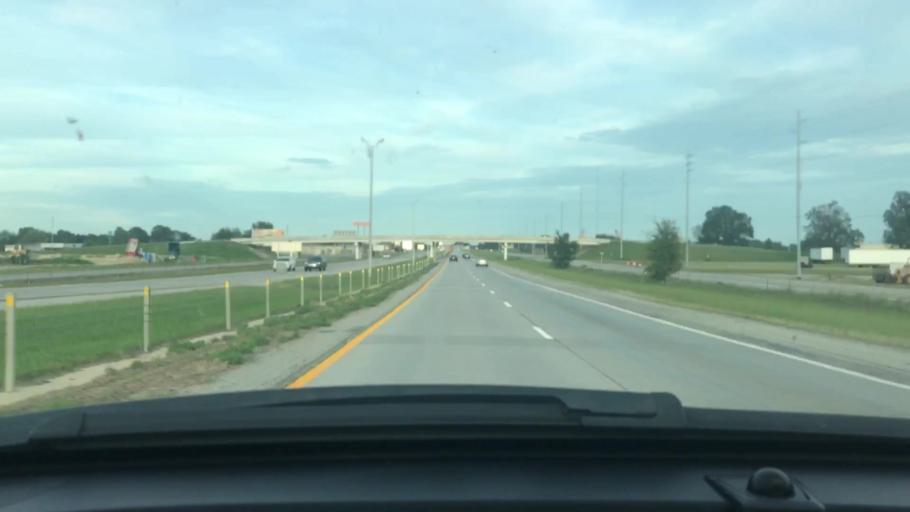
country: US
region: Arkansas
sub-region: Craighead County
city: Jonesboro
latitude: 35.8069
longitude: -90.6546
